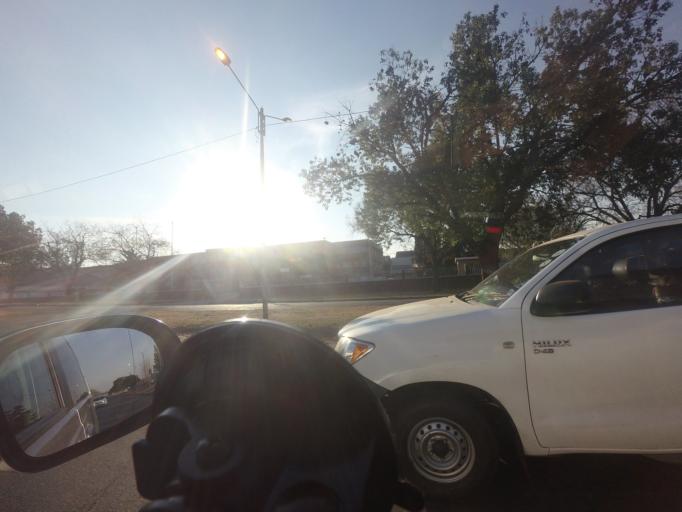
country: ZA
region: Gauteng
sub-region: Sedibeng District Municipality
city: Vereeniging
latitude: -26.6611
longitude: 27.9473
